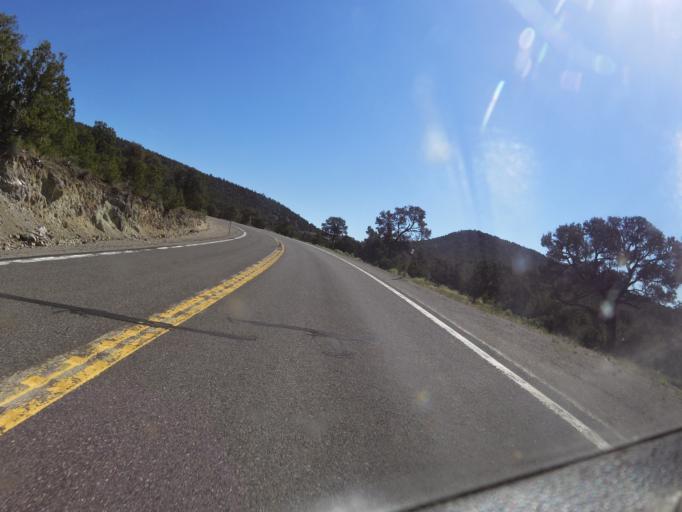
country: US
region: Nevada
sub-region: White Pine County
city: Ely
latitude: 38.8141
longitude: -115.2956
